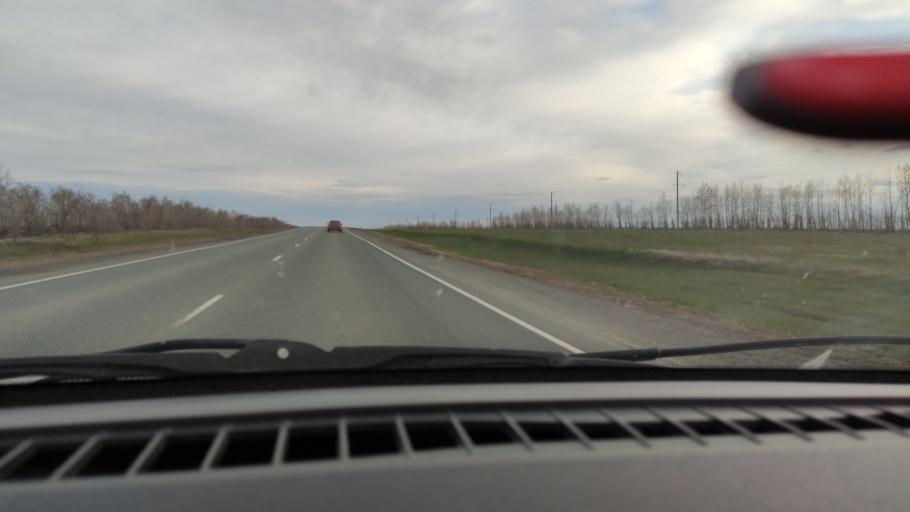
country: RU
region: Orenburg
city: Sakmara
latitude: 52.1416
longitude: 55.2839
